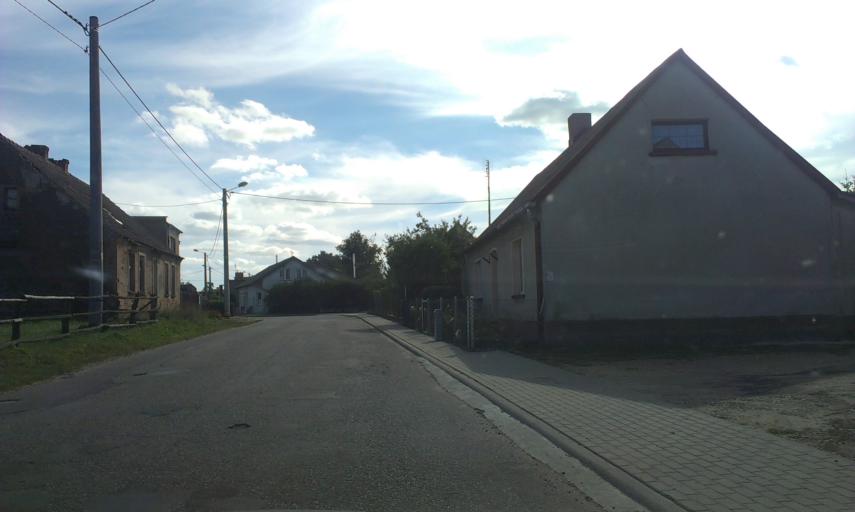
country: PL
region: Greater Poland Voivodeship
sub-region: Powiat zlotowski
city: Zlotow
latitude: 53.3077
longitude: 17.1273
